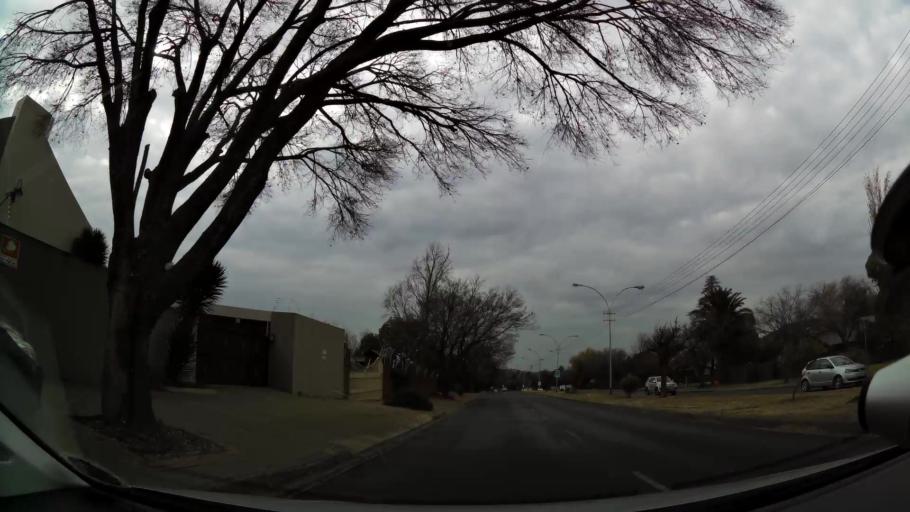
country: ZA
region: Orange Free State
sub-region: Mangaung Metropolitan Municipality
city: Bloemfontein
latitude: -29.0961
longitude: 26.2131
